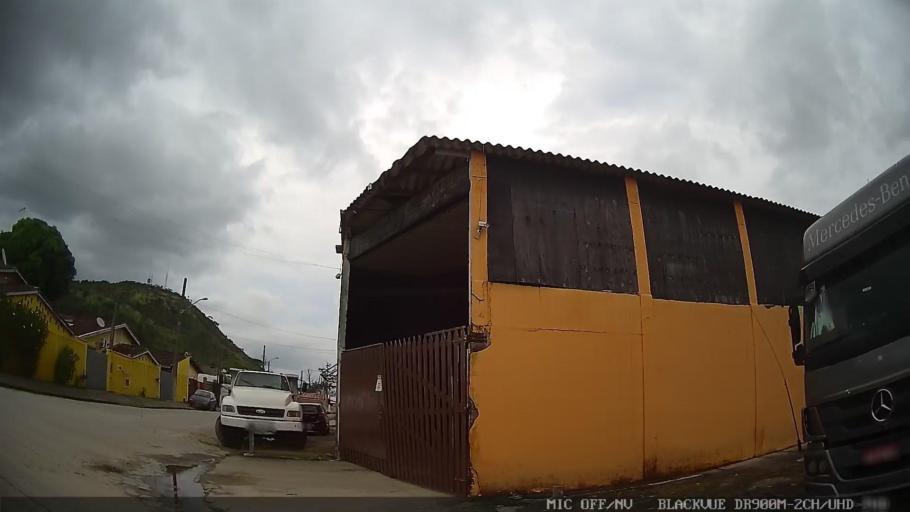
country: BR
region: Sao Paulo
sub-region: Caraguatatuba
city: Caraguatatuba
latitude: -23.6168
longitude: -45.3900
